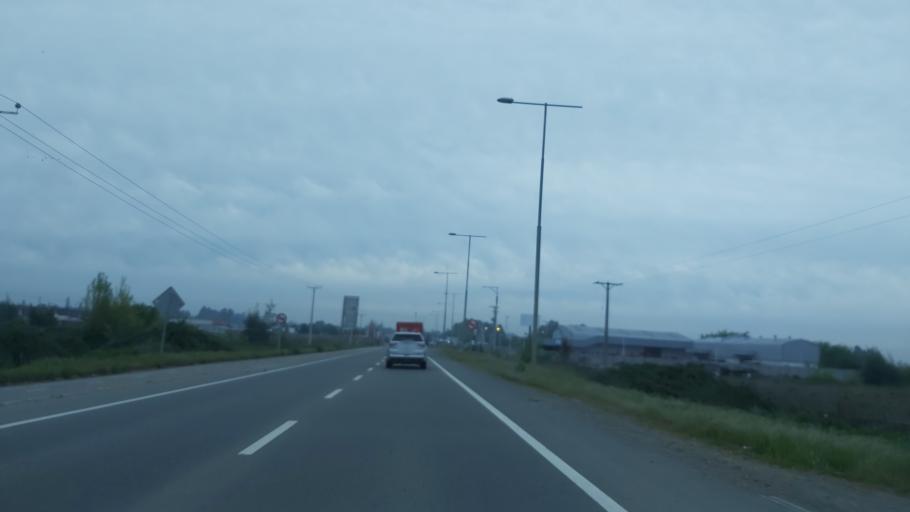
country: CL
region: Maule
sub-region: Provincia de Linares
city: Linares
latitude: -35.8332
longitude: -71.6198
